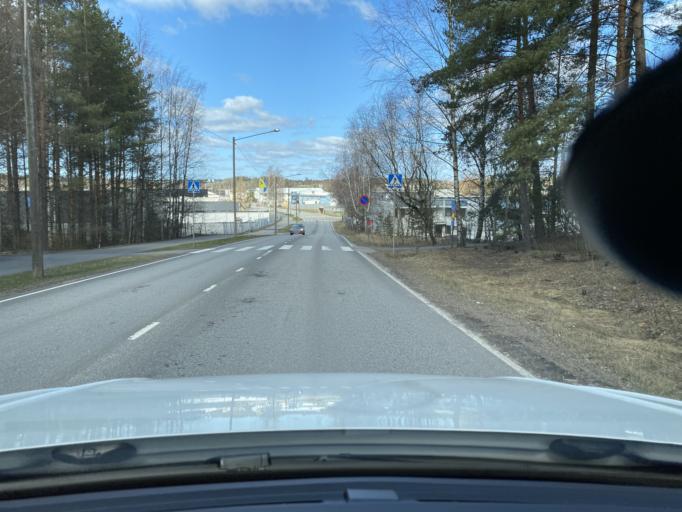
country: FI
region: Varsinais-Suomi
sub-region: Turku
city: Turku
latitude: 60.4798
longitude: 22.3148
